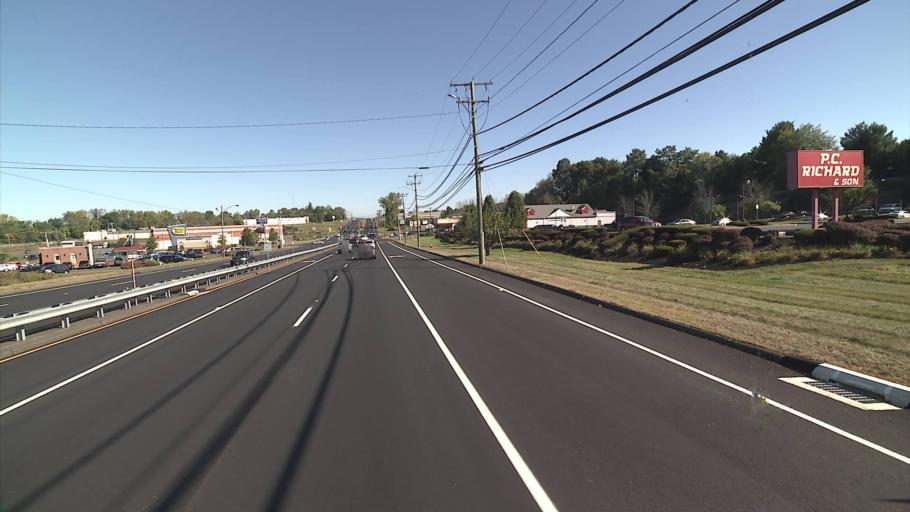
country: US
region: Connecticut
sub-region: Hartford County
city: Newington
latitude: 41.6533
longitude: -72.7267
